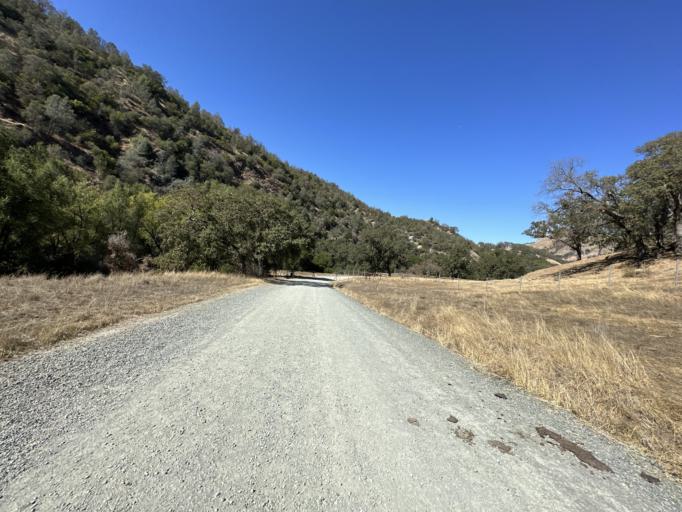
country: US
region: California
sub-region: Santa Clara County
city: Milpitas
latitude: 37.5057
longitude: -121.8276
